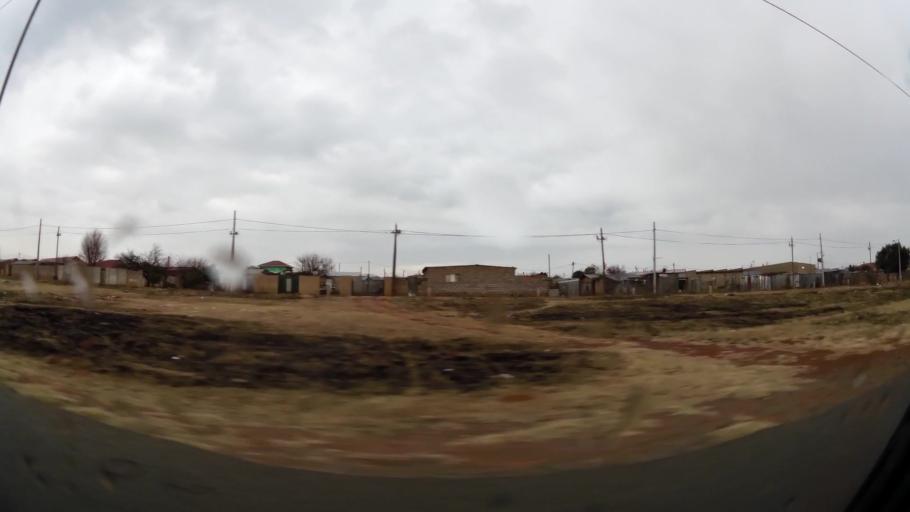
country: ZA
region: Gauteng
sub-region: West Rand District Municipality
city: Randfontein
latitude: -26.1730
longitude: 27.7816
